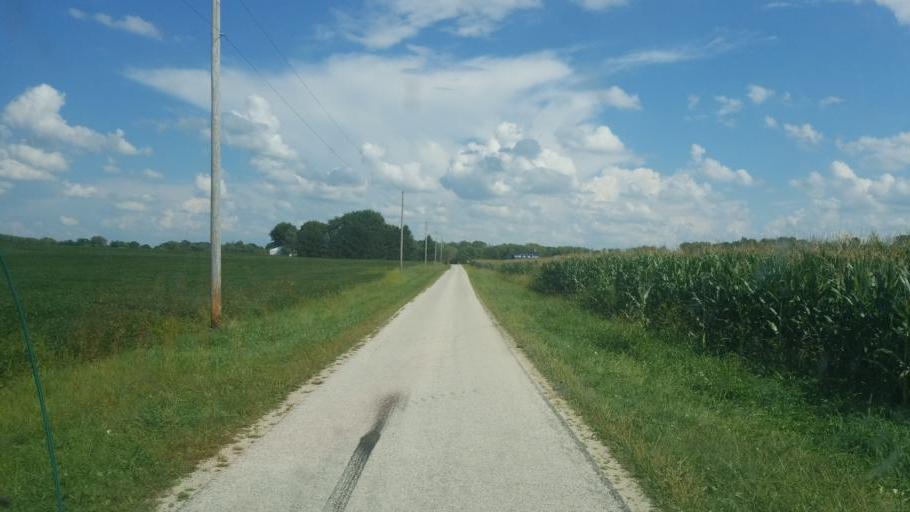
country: US
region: Ohio
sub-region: Seneca County
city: Tiffin
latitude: 40.9784
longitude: -83.2223
